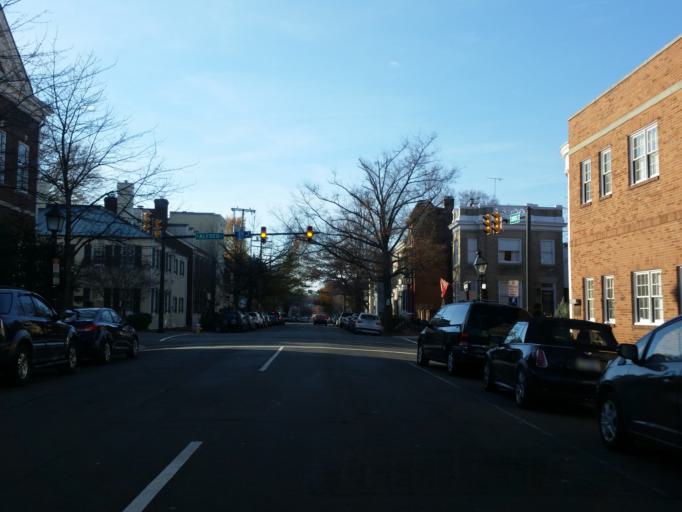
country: US
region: Virginia
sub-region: City of Alexandria
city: Alexandria
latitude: 38.8065
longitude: -77.0485
